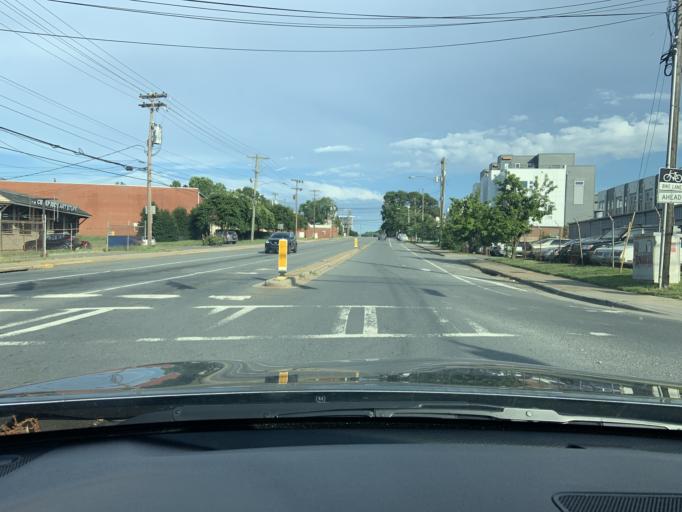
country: US
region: North Carolina
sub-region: Mecklenburg County
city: Charlotte
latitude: 35.2055
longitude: -80.8695
